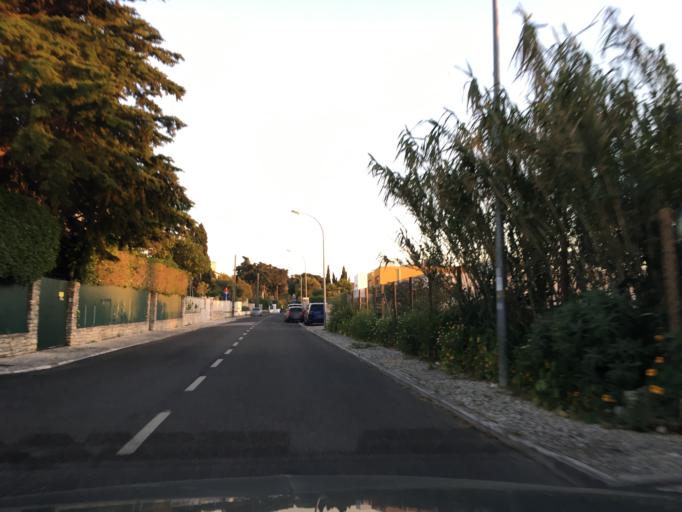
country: PT
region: Lisbon
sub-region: Oeiras
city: Terrugem
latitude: 38.7038
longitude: -9.2883
